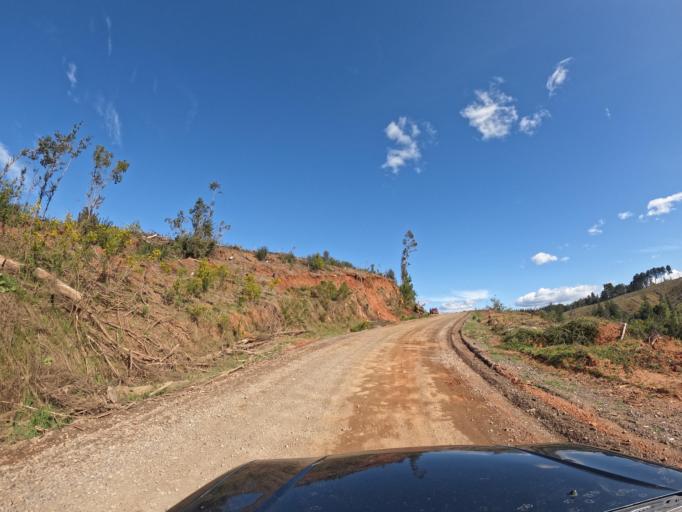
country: CL
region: Biobio
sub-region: Provincia de Biobio
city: La Laja
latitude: -37.0832
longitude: -72.8330
